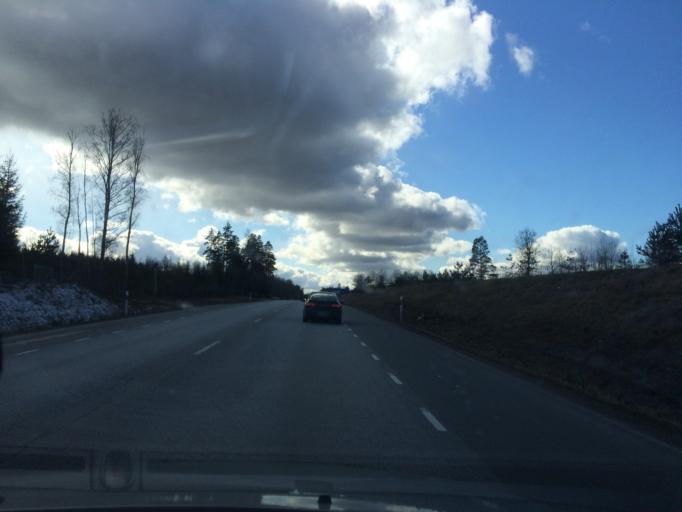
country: SE
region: Vaestra Goetaland
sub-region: Mariestads Kommun
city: Mariestad
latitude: 58.6449
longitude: 13.7103
